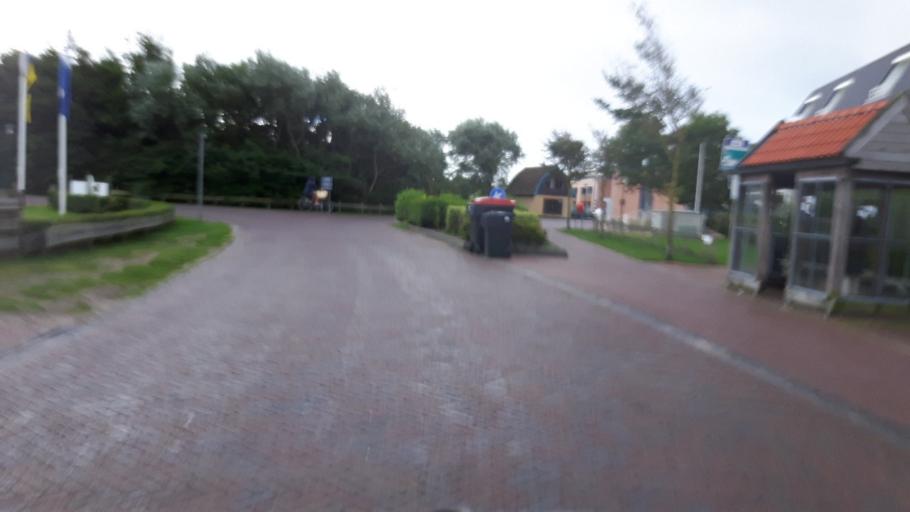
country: NL
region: Friesland
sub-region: Gemeente Ameland
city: Nes
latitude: 53.4521
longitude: 5.7759
